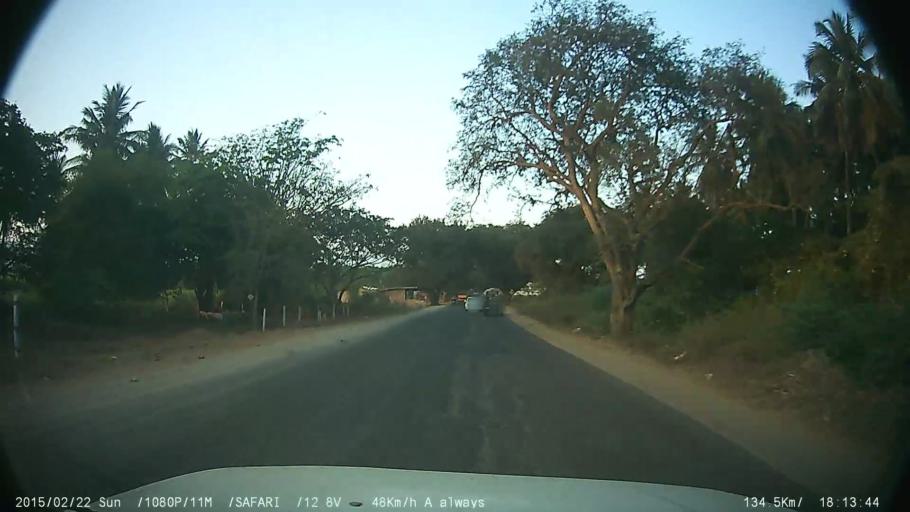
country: IN
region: Tamil Nadu
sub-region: Theni
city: Chinnamanur
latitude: 9.8530
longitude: 77.3860
